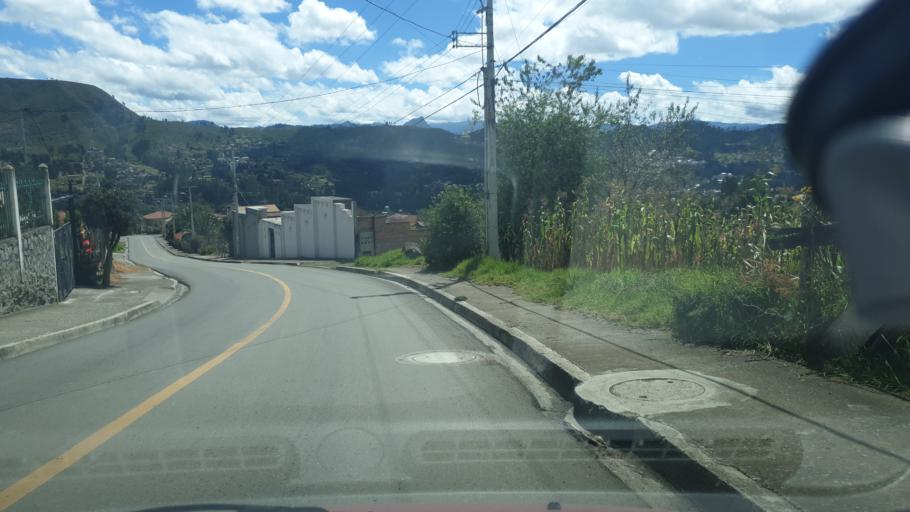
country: EC
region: Azuay
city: Llacao
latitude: -2.8608
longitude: -78.9075
